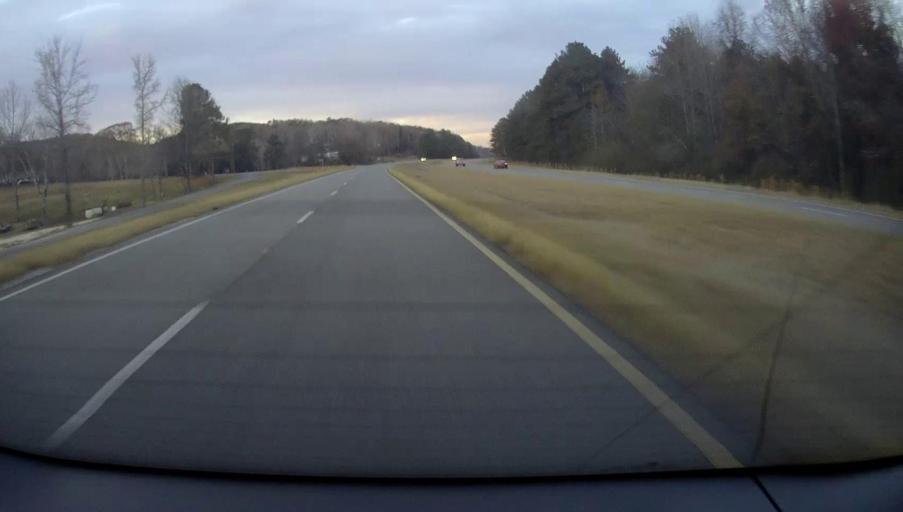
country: US
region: Alabama
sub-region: Etowah County
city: Glencoe
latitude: 33.9139
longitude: -85.9132
